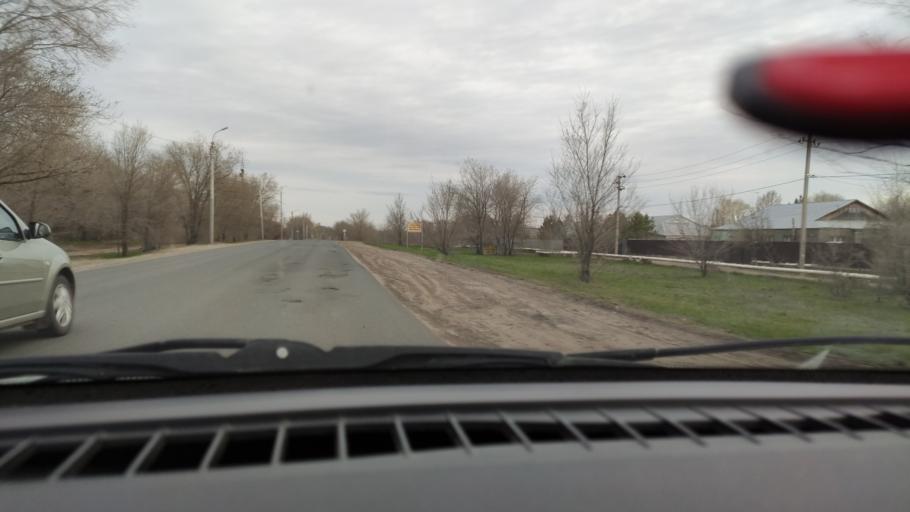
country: RU
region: Orenburg
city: Tatarskaya Kargala
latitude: 51.8743
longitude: 55.1462
